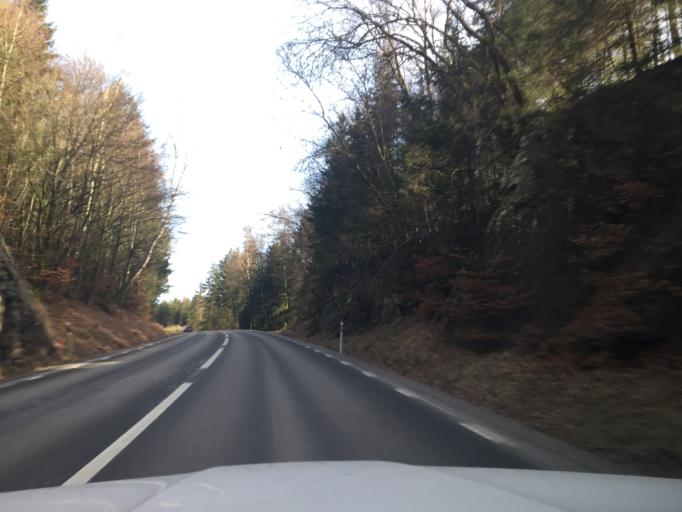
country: SE
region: Halland
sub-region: Varbergs Kommun
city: Tvaaker
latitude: 57.1485
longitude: 12.5976
